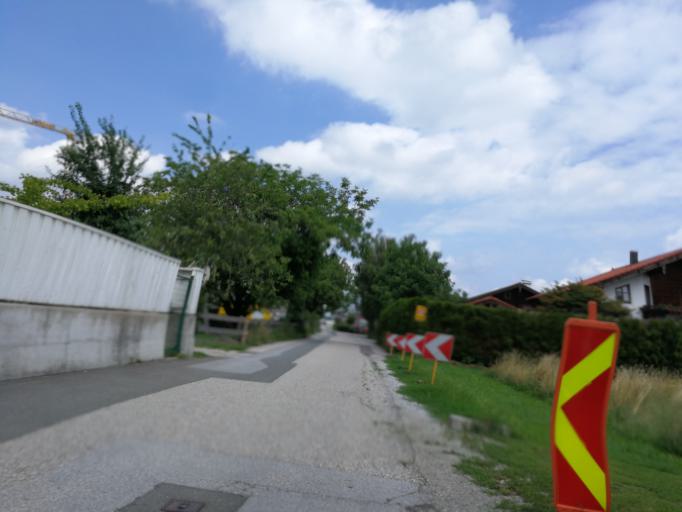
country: DE
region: Bavaria
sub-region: Upper Bavaria
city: Freilassing
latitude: 47.8081
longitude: 12.9859
